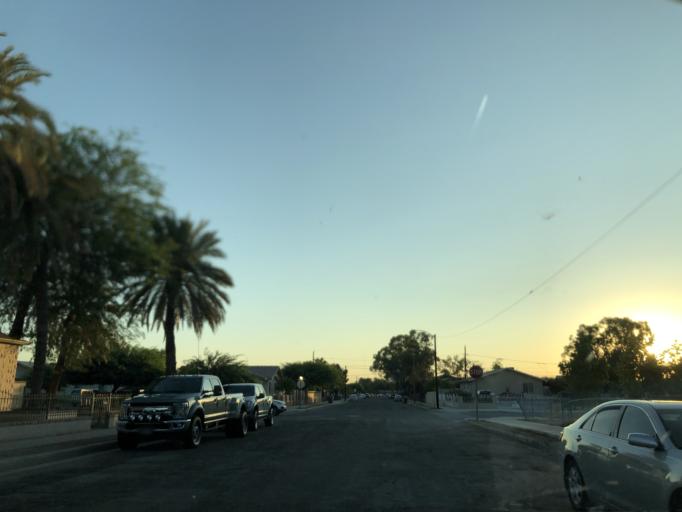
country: US
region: Arizona
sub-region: Yuma County
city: Yuma
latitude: 32.7234
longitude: -114.6290
